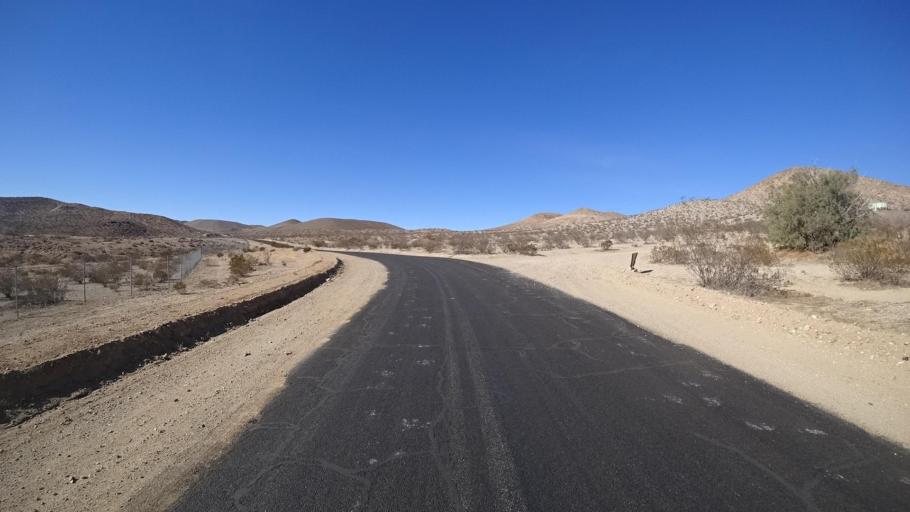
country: US
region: California
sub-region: Kern County
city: Ridgecrest
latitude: 35.3541
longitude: -117.6244
